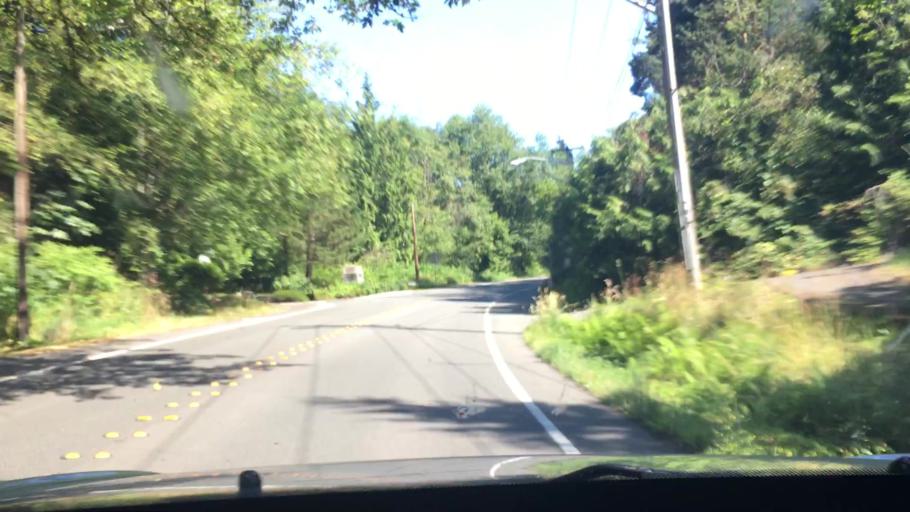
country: US
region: Washington
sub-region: King County
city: Newcastle
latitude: 47.5430
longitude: -122.1303
